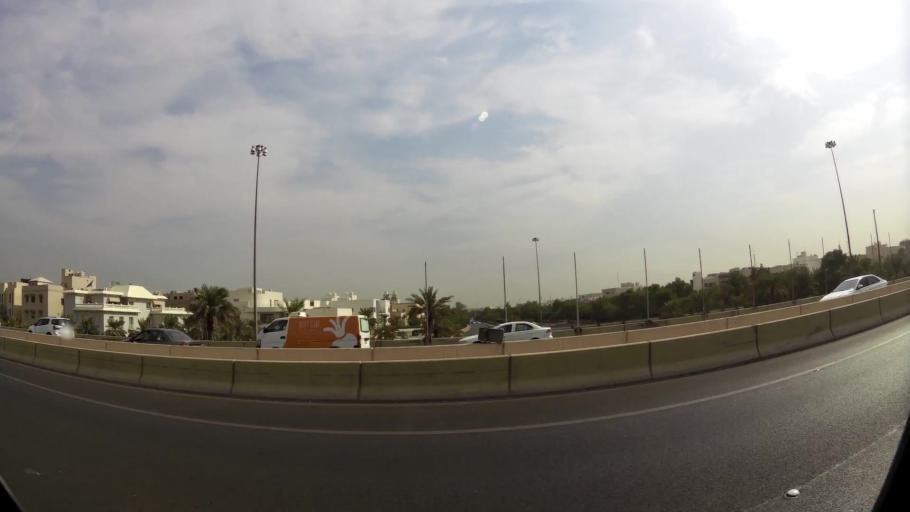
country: KW
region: Al Asimah
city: Ash Shamiyah
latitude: 29.3318
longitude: 47.9712
